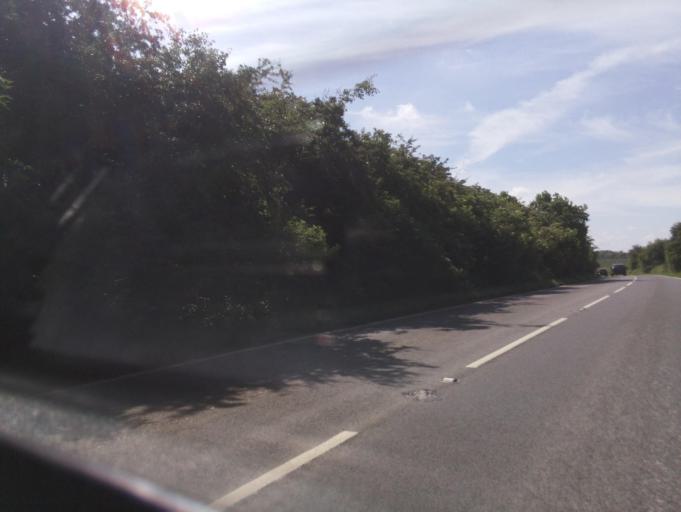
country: GB
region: England
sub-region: North Lincolnshire
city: Manton
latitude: 53.5091
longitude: -0.5824
